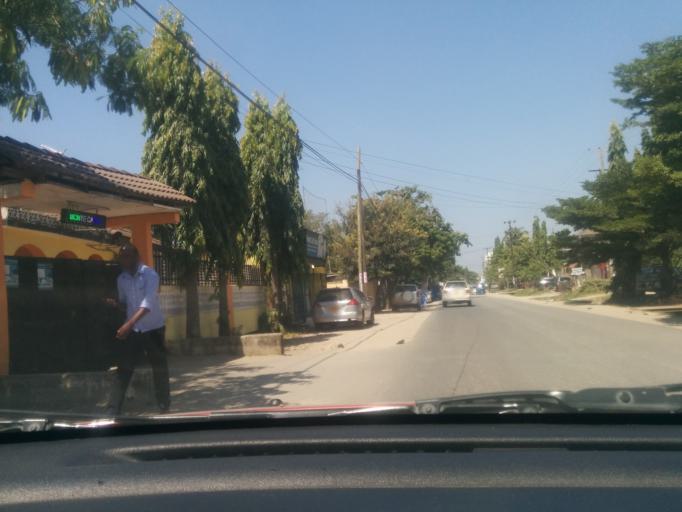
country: TZ
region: Dar es Salaam
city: Magomeni
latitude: -6.7729
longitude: 39.2246
